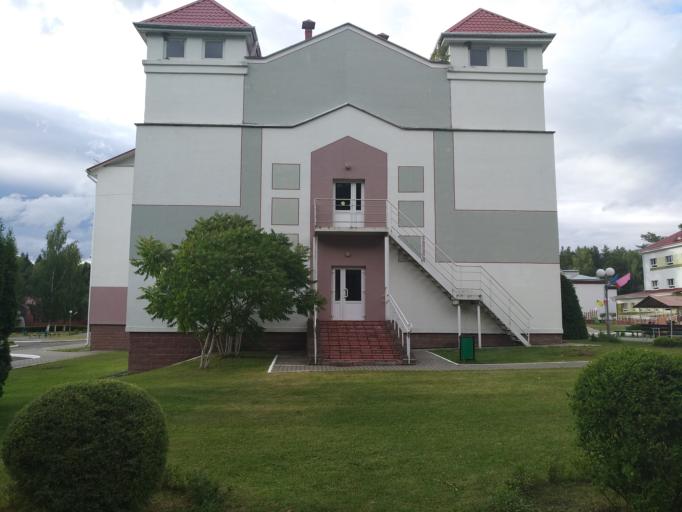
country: BY
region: Grodnenskaya
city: Vishnyeva
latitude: 54.6359
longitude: 26.4166
